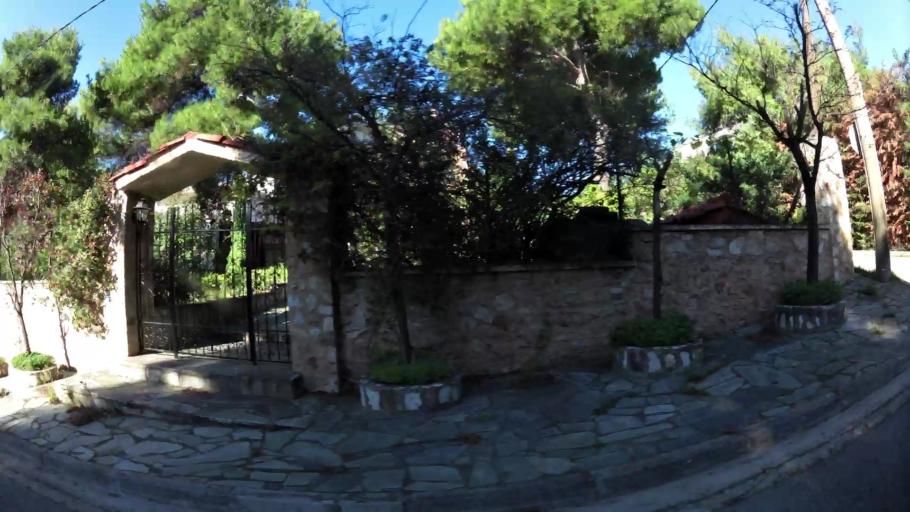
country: GR
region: Attica
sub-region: Nomarchia Anatolikis Attikis
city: Drosia
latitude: 38.1276
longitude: 23.8720
